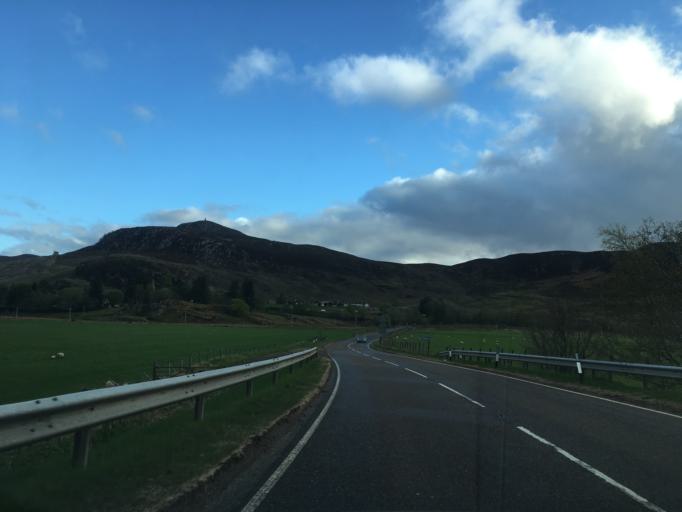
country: GB
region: Scotland
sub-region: Highland
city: Kingussie
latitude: 57.0182
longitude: -4.2841
